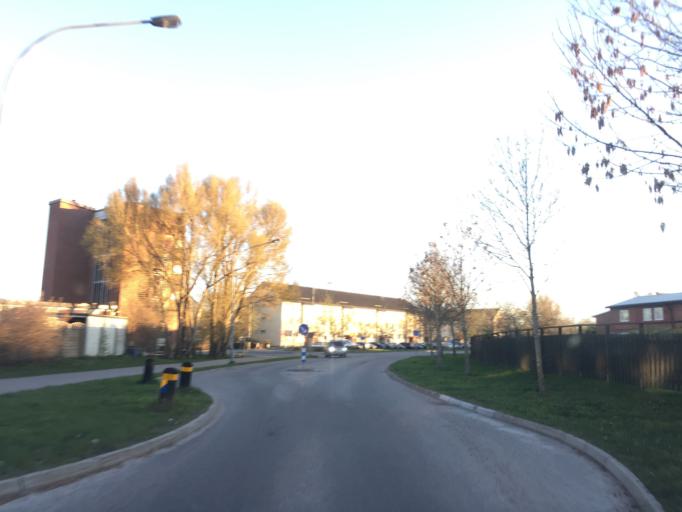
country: SE
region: OErebro
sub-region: Orebro Kommun
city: Orebro
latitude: 59.2599
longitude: 15.2371
